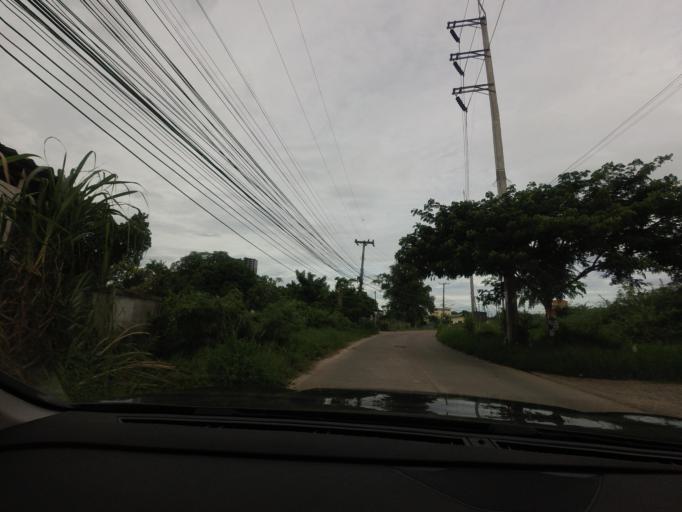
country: TH
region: Prachuap Khiri Khan
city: Hua Hin
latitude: 12.5381
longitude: 99.9543
